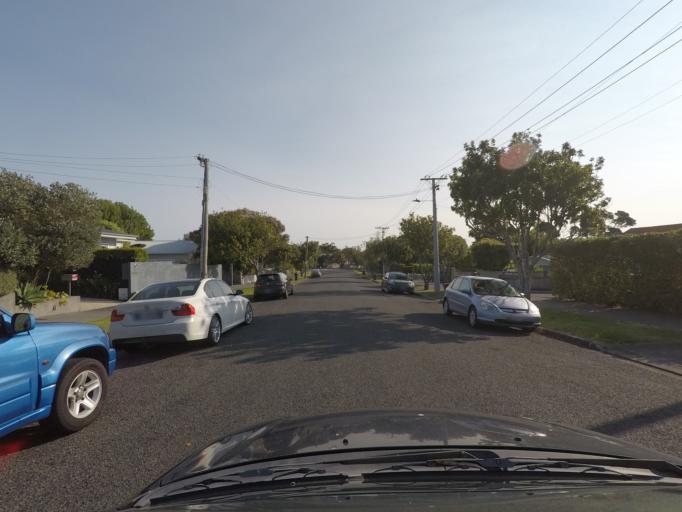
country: NZ
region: Auckland
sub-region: Auckland
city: Rosebank
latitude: -36.8589
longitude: 174.7010
